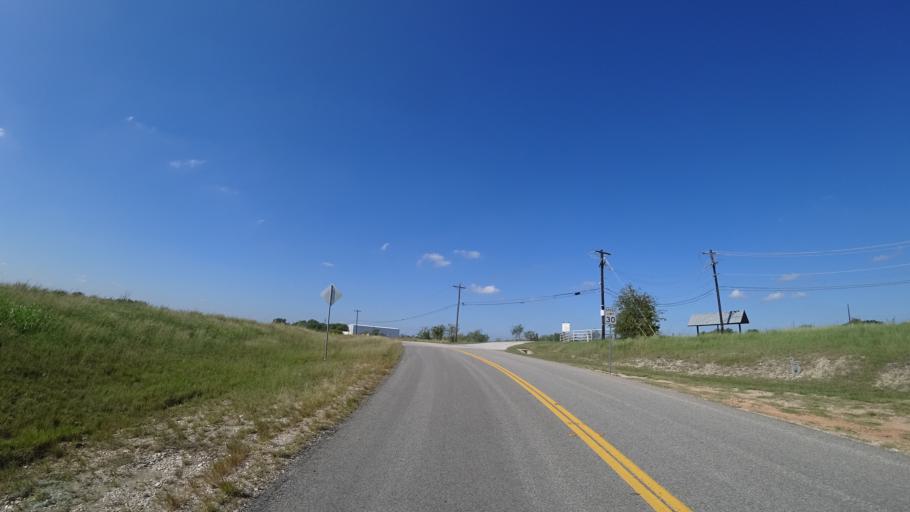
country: US
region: Texas
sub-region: Travis County
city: Manor
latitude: 30.3372
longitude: -97.6029
